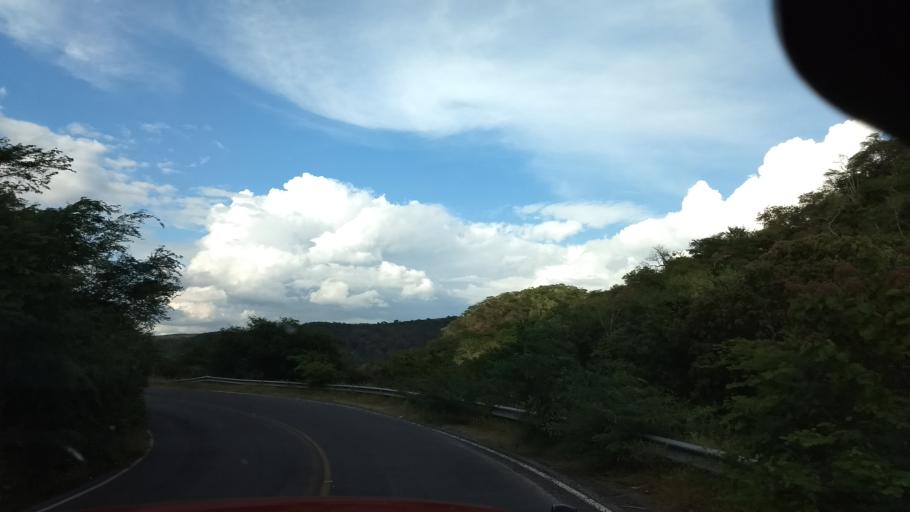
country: MX
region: Colima
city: Suchitlan
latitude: 19.4559
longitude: -103.8213
